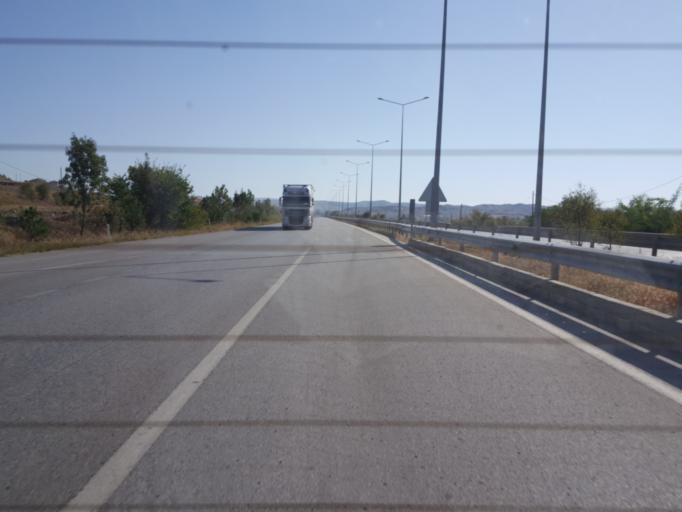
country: TR
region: Corum
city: Sungurlu
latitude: 40.1769
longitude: 34.4464
